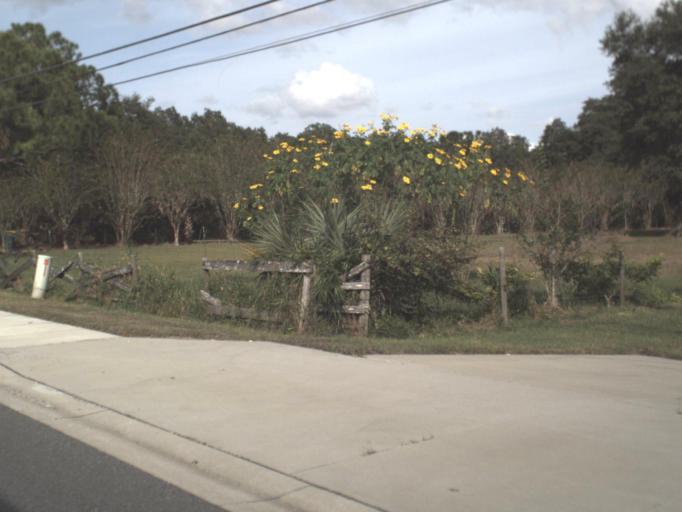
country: US
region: Florida
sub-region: Osceola County
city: Saint Cloud
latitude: 28.3363
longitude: -81.2281
